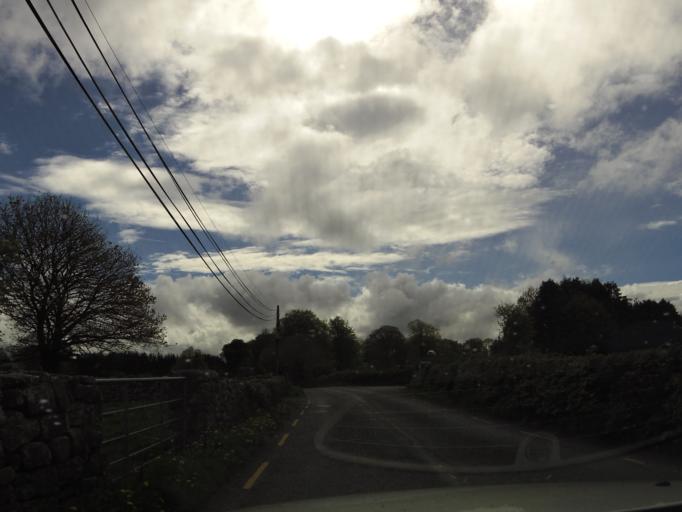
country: IE
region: Connaught
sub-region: Maigh Eo
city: Ballinrobe
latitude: 53.5514
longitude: -9.2622
